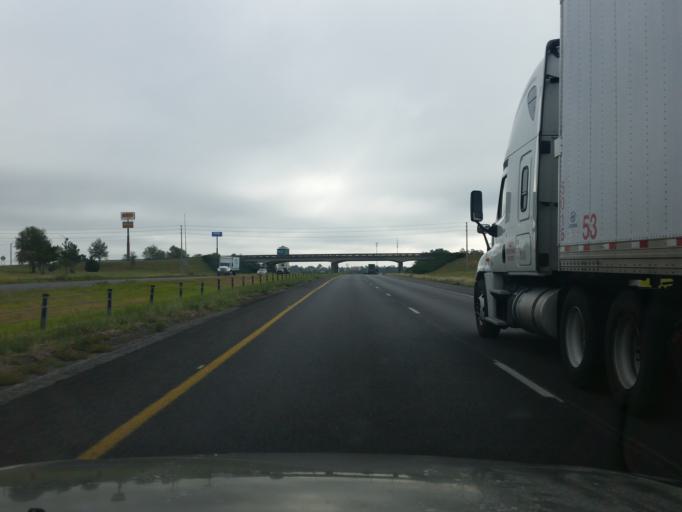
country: US
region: Alabama
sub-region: Baldwin County
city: Spanish Fort
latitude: 30.6630
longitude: -87.8552
